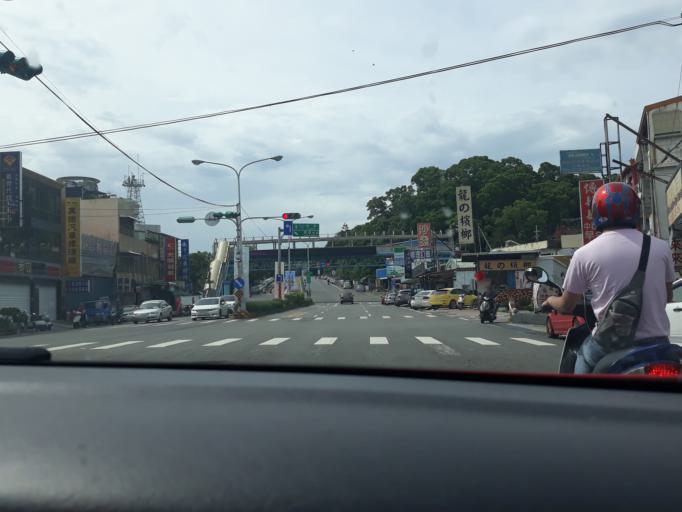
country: TW
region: Taiwan
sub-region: Miaoli
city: Miaoli
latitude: 24.5522
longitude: 120.8140
